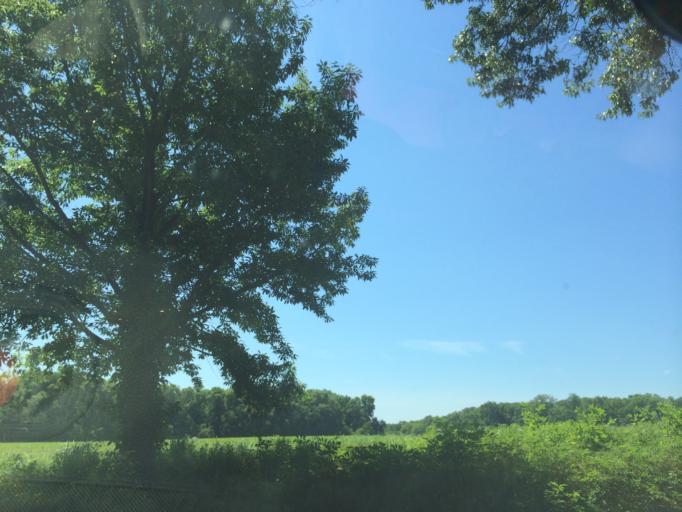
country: US
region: Maryland
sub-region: Queen Anne's County
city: Grasonville
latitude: 38.8909
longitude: -76.1596
